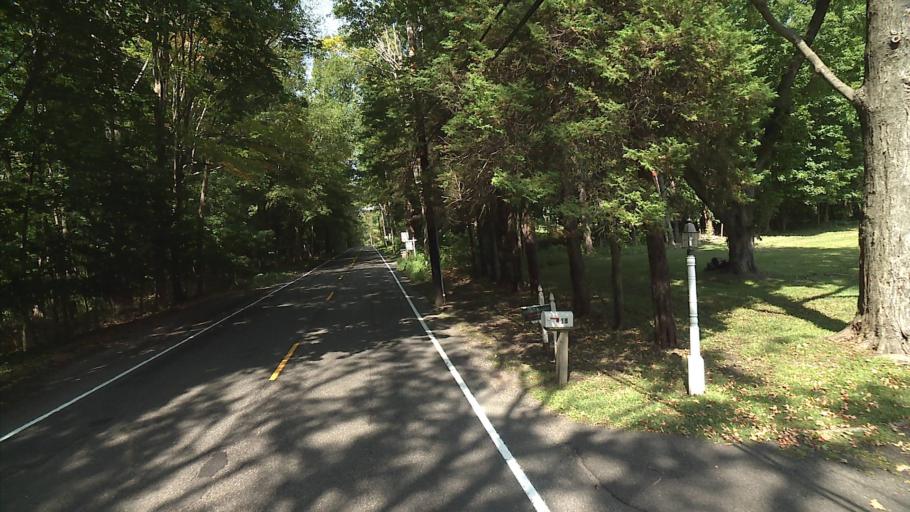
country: US
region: Connecticut
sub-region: Fairfield County
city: Georgetown
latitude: 41.2872
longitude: -73.3428
